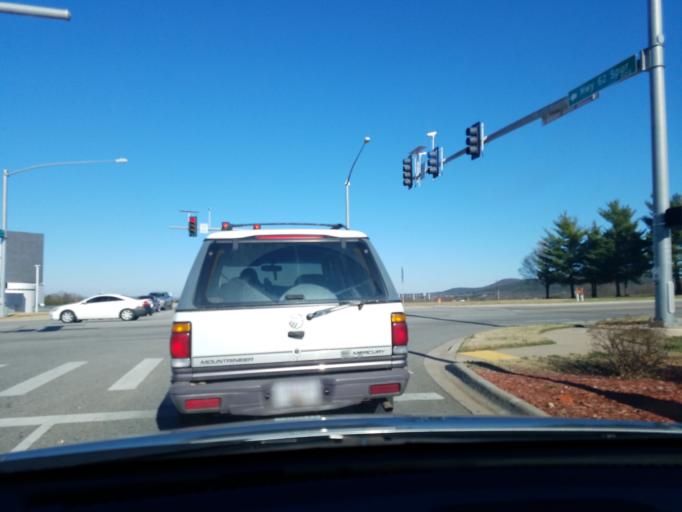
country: US
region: Arkansas
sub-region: Carroll County
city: Berryville
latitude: 36.3773
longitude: -93.5849
